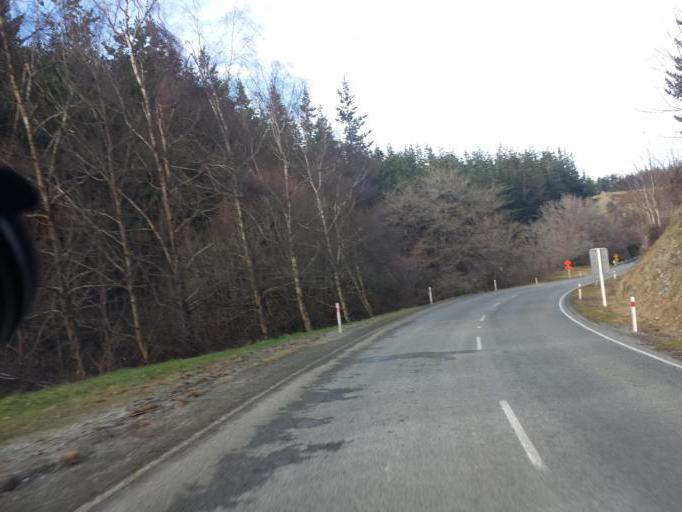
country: NZ
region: Canterbury
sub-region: Timaru District
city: Pleasant Point
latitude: -44.1253
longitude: 171.0857
